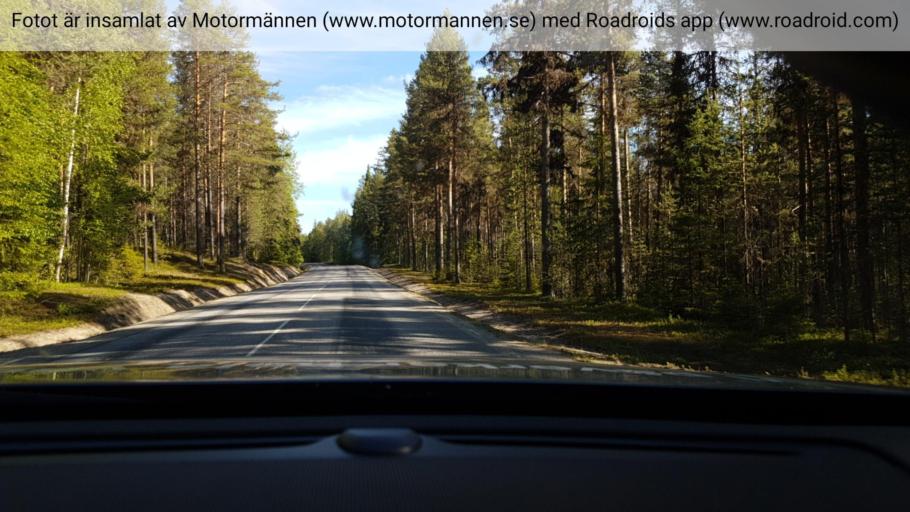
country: SE
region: Vaesterbotten
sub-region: Norsjo Kommun
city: Norsjoe
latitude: 64.6494
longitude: 19.2784
